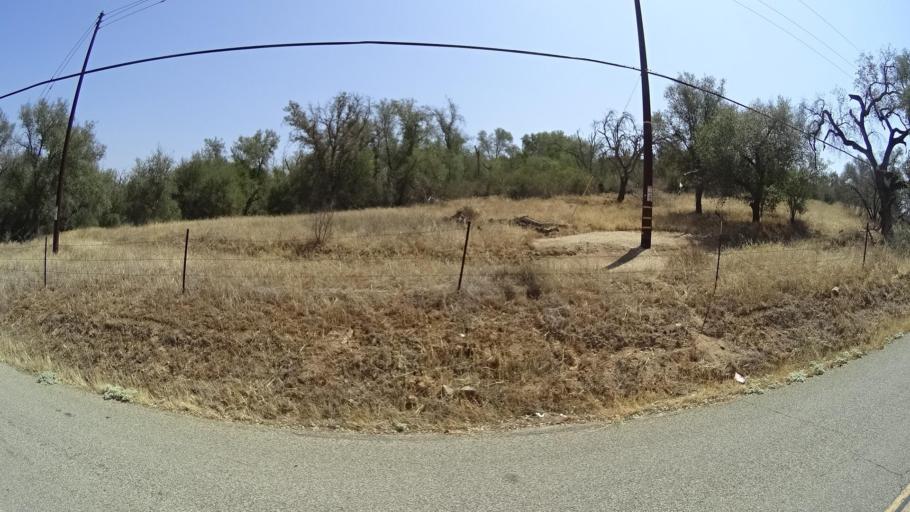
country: US
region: California
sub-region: San Diego County
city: Fallbrook
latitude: 33.4443
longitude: -117.3249
